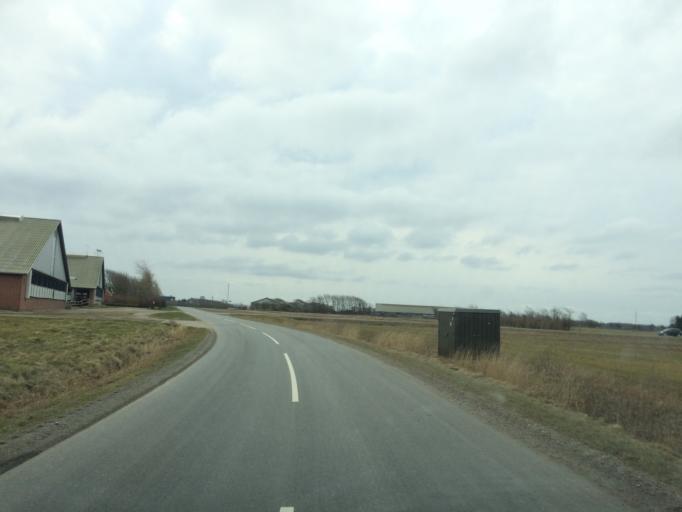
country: DK
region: South Denmark
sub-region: Varde Kommune
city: Oksbol
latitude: 55.7874
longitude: 8.3135
